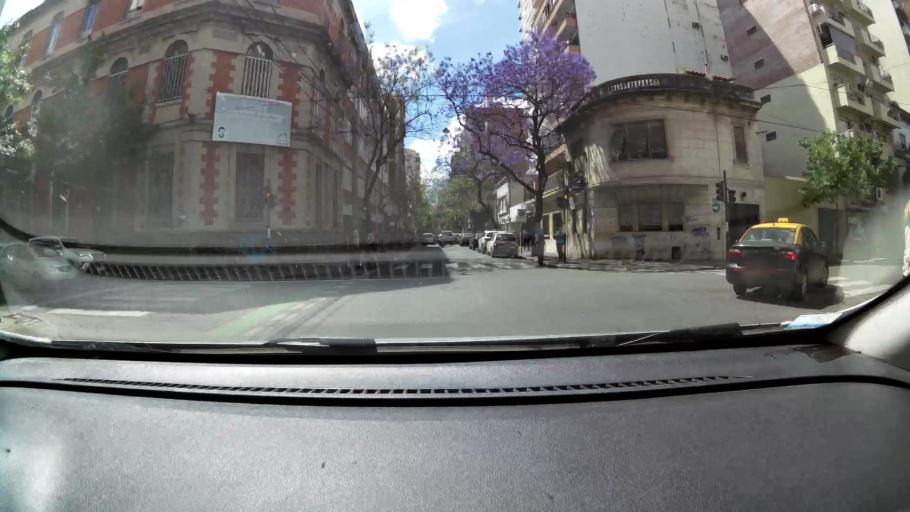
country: AR
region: Santa Fe
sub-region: Departamento de Rosario
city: Rosario
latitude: -32.9380
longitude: -60.6448
